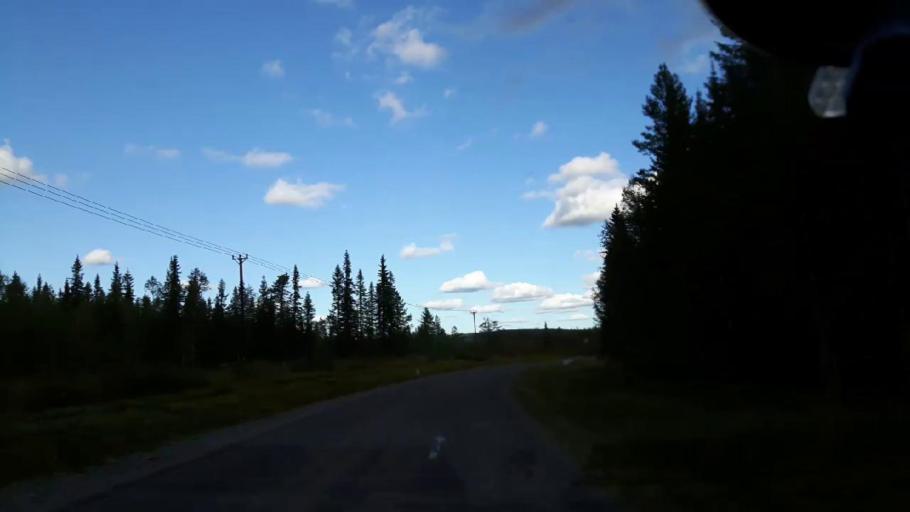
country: SE
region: Jaemtland
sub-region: Stroemsunds Kommun
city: Stroemsund
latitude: 63.4292
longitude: 15.9020
